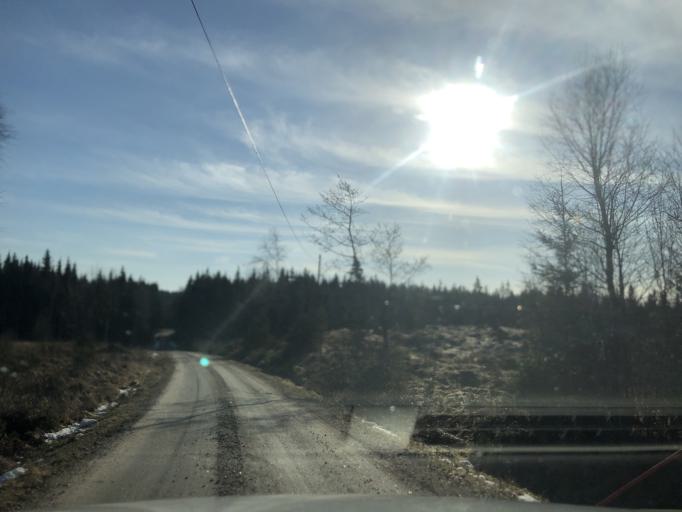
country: SE
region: Vaestra Goetaland
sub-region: Ulricehamns Kommun
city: Ulricehamn
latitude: 57.7920
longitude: 13.4692
